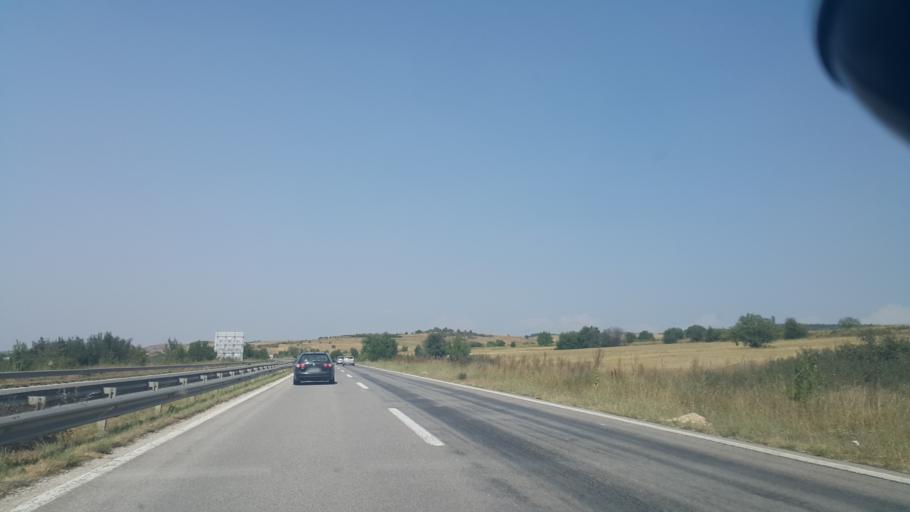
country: MK
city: Miladinovci
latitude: 41.9675
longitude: 21.6422
